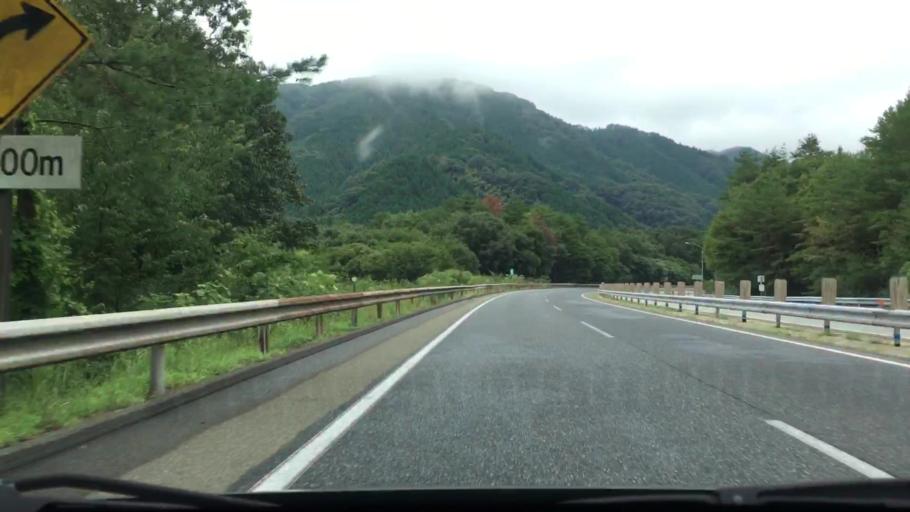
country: JP
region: Hiroshima
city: Shobara
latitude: 34.8579
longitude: 133.1006
